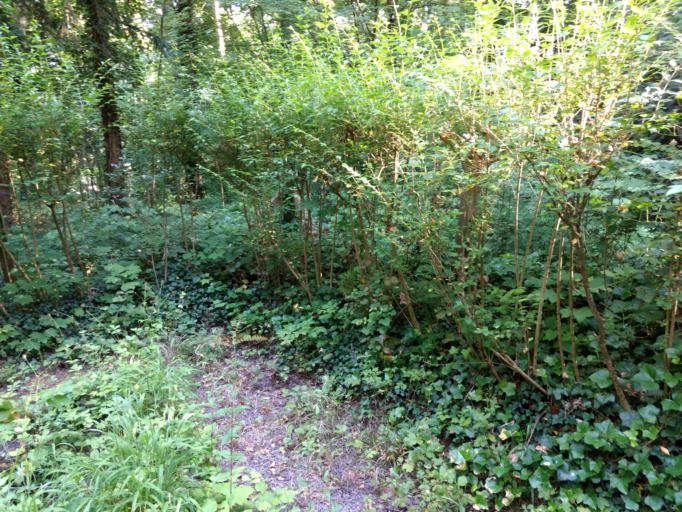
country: DE
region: Saarland
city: Beckingen
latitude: 49.3894
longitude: 6.6975
